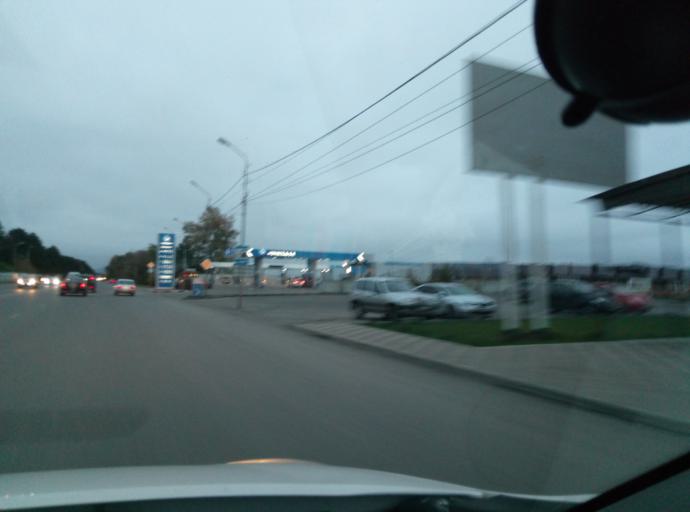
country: RU
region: Stavropol'skiy
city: Yessentukskaya
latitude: 44.0544
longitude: 42.9101
